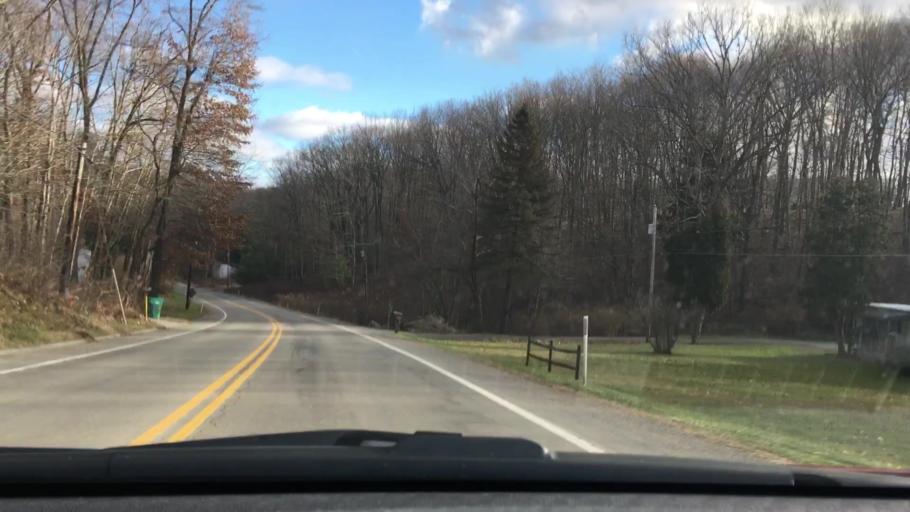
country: US
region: Pennsylvania
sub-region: Westmoreland County
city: Avonmore
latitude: 40.6450
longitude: -79.3414
